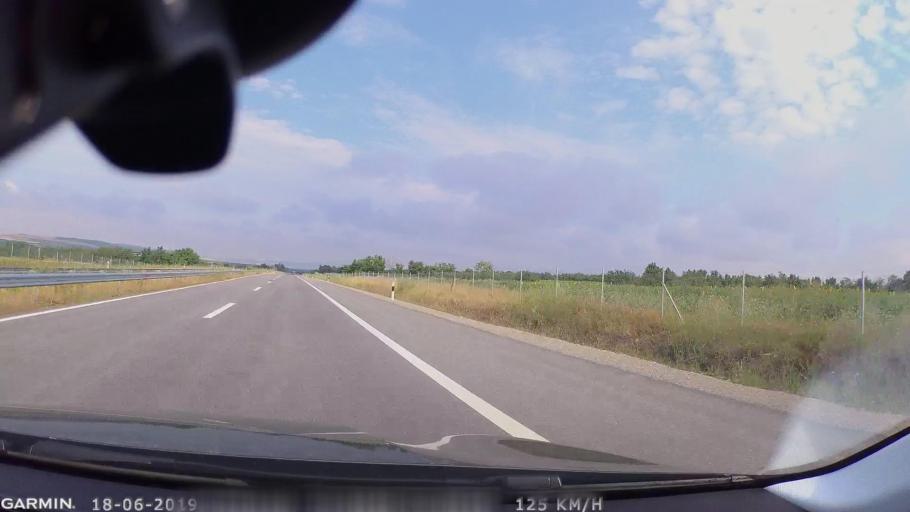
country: MK
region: Sveti Nikole
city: Sveti Nikole
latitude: 41.8285
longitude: 22.0022
